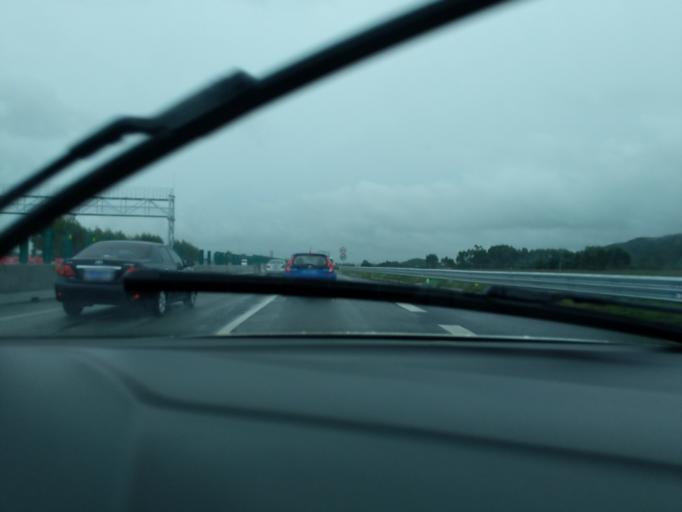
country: CN
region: Guangdong
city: Yueshan
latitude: 22.4582
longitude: 112.6850
